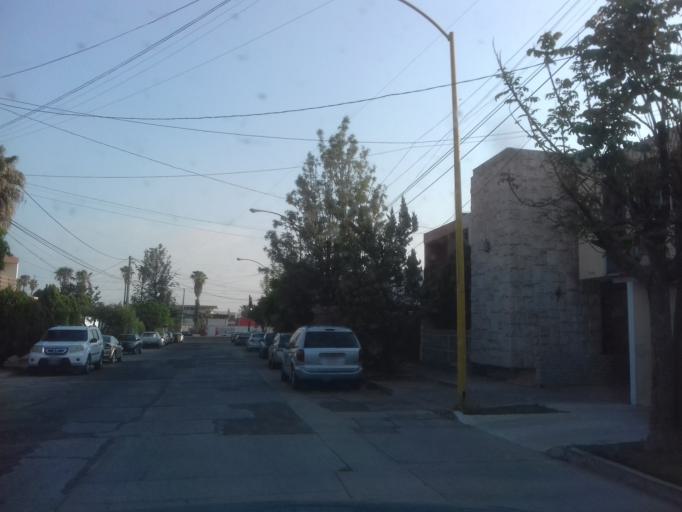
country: MX
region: Aguascalientes
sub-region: Aguascalientes
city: Aguascalientes
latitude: 21.8645
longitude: -102.2916
